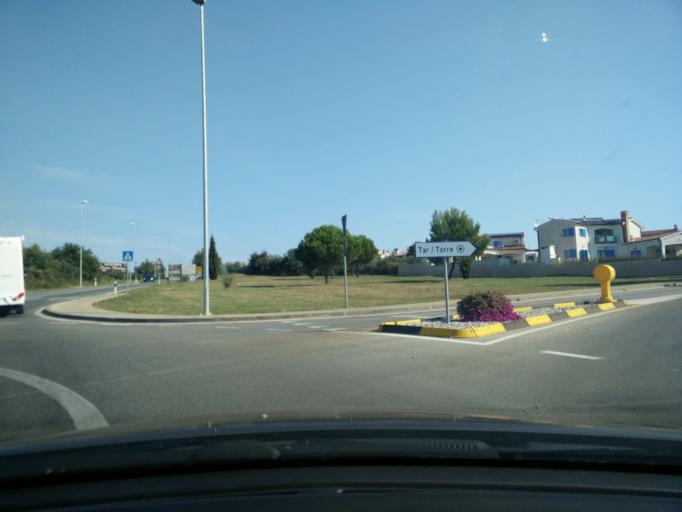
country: HR
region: Istarska
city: Novigrad
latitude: 45.2952
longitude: 13.6219
